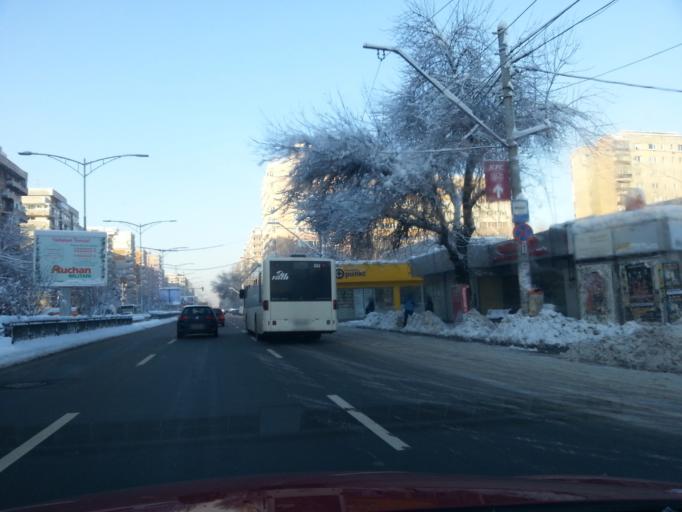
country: RO
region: Ilfov
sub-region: Comuna Chiajna
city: Rosu
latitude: 44.4341
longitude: 26.0200
